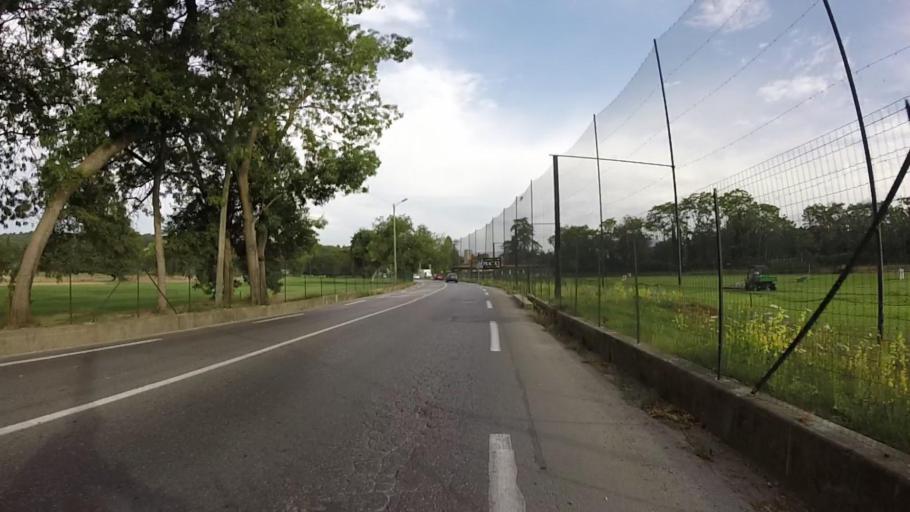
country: FR
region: Provence-Alpes-Cote d'Azur
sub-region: Departement des Alpes-Maritimes
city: Biot
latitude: 43.6161
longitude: 7.1068
